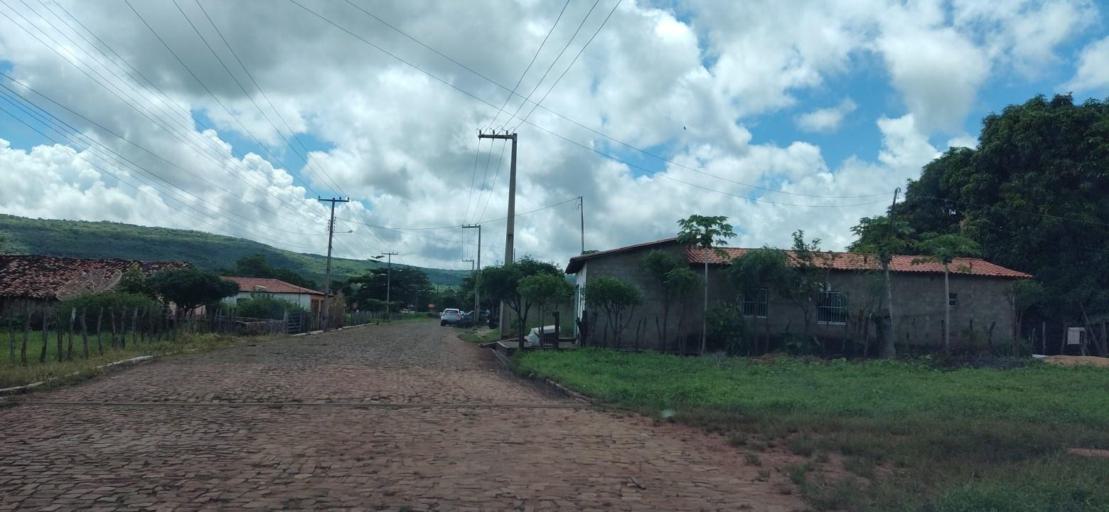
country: BR
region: Piaui
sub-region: Valenca Do Piaui
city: Valenca do Piaui
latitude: -6.1119
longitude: -41.8015
